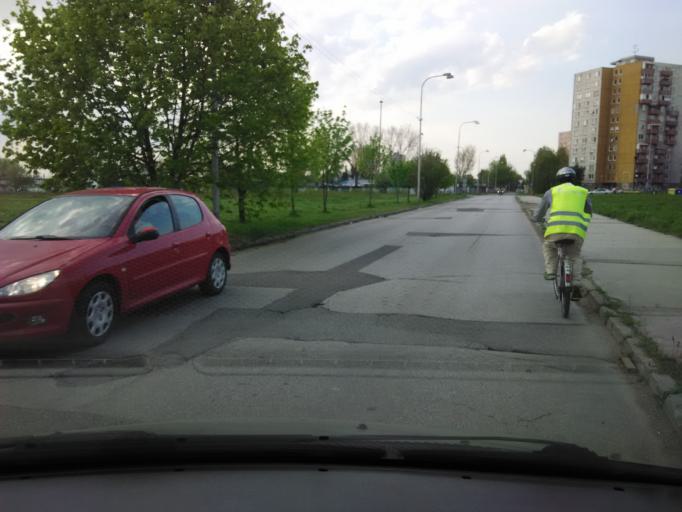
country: SK
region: Nitriansky
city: Levice
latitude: 48.2057
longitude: 18.6026
